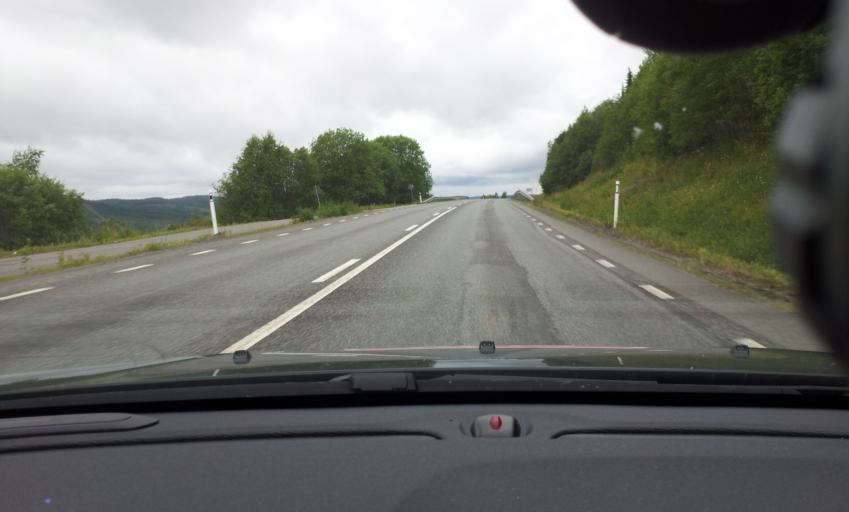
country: SE
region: Jaemtland
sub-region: Are Kommun
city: Are
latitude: 63.3951
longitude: 12.9455
